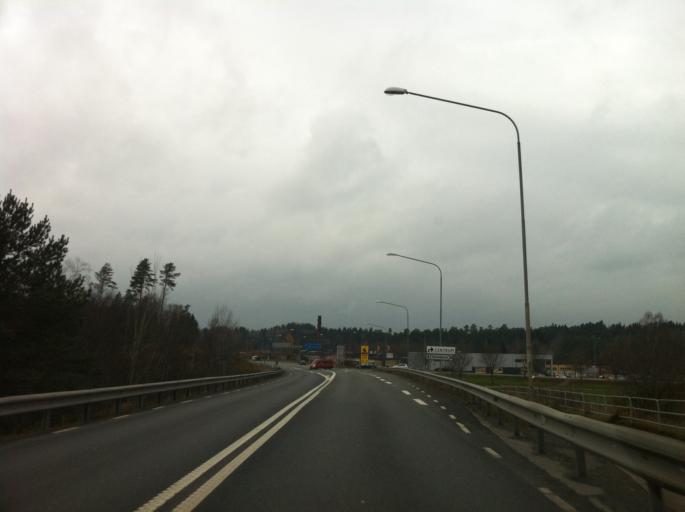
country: SE
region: Joenkoeping
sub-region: Savsjo Kommun
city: Saevsjoe
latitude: 57.3939
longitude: 14.6904
